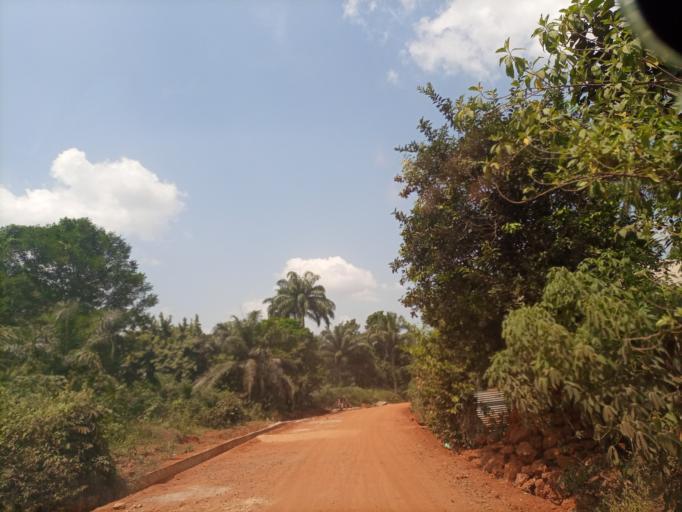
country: NG
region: Enugu
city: Obollo-Afor
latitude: 6.8647
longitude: 7.4734
